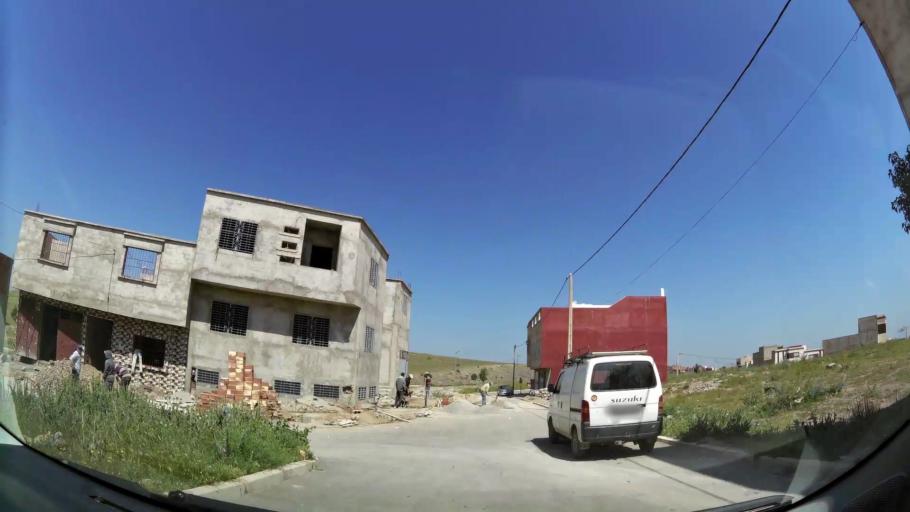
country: MA
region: Oriental
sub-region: Oujda-Angad
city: Oujda
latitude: 34.6728
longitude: -1.9460
